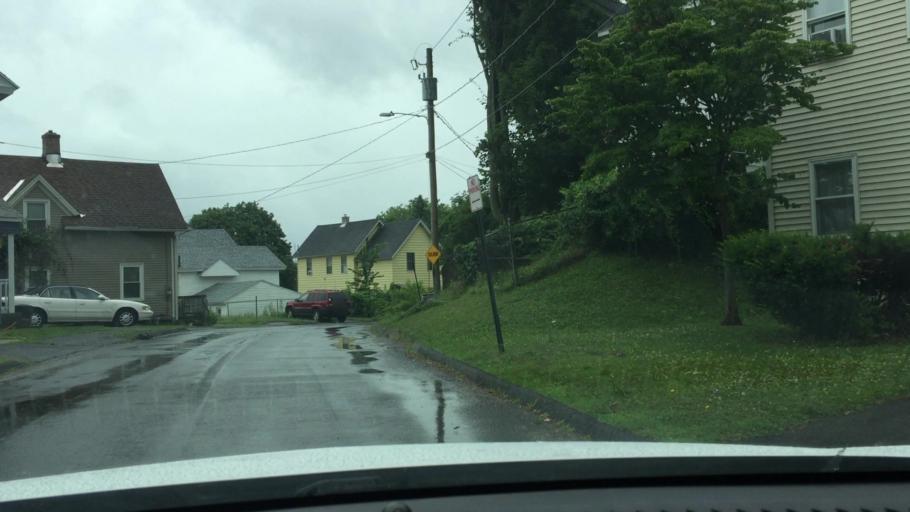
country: US
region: Massachusetts
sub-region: Berkshire County
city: Pittsfield
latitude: 42.4519
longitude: -73.2582
